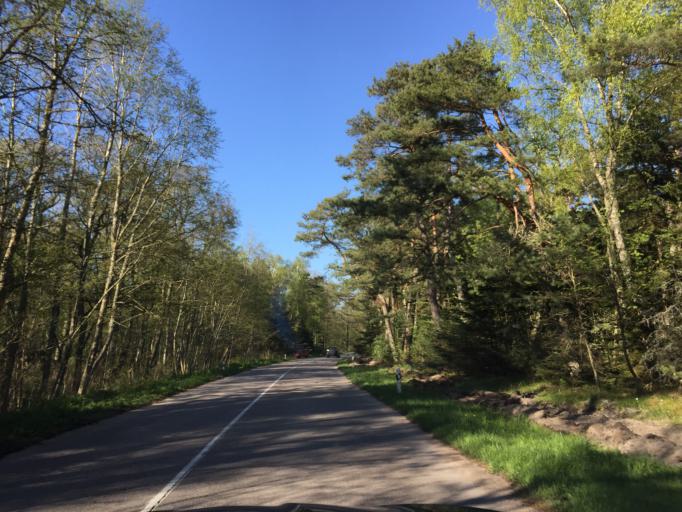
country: LT
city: Nida
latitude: 55.1905
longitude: 20.8588
